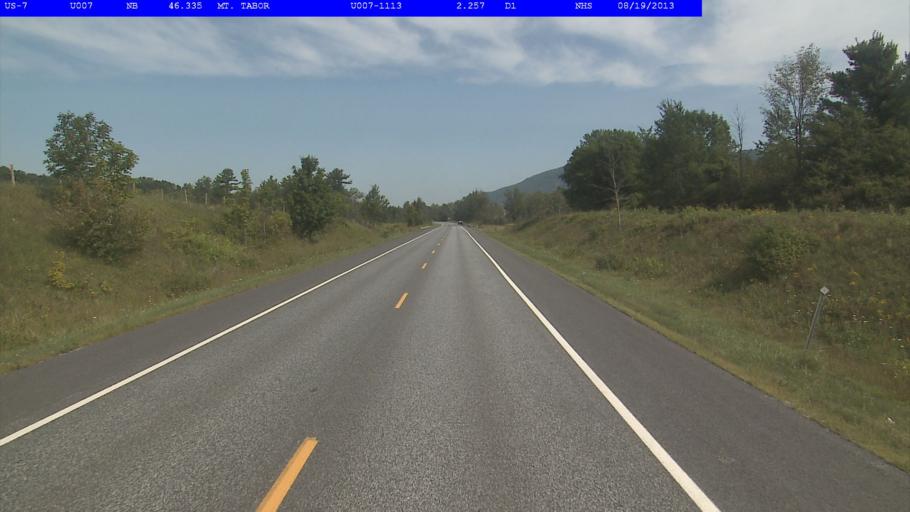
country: US
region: Vermont
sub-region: Bennington County
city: Manchester Center
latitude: 43.3375
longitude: -72.9921
